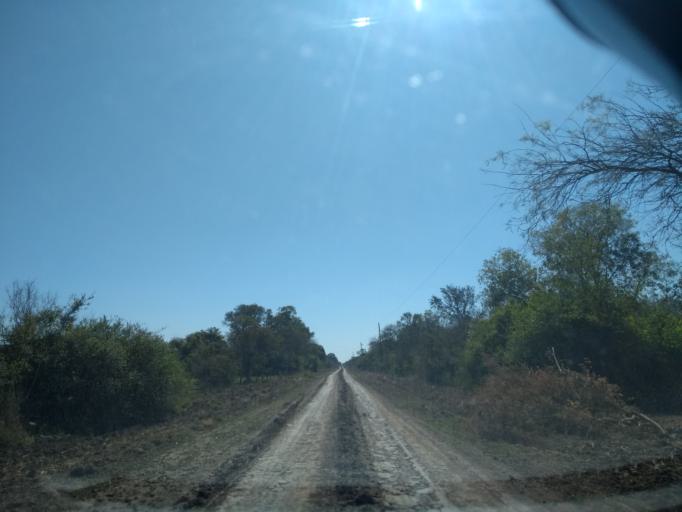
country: AR
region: Chaco
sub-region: Departamento de Quitilipi
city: Quitilipi
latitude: -26.7550
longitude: -60.2423
